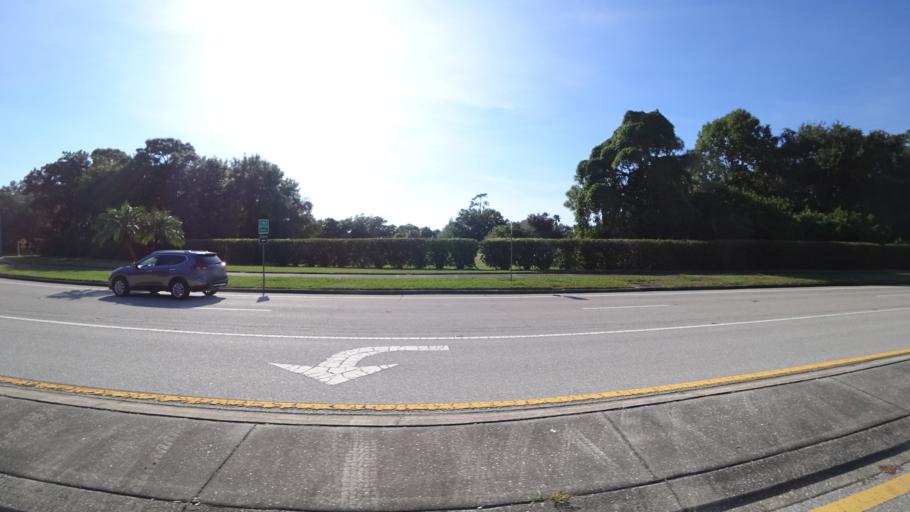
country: US
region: Florida
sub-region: Sarasota County
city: Desoto Lakes
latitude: 27.4419
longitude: -82.4699
